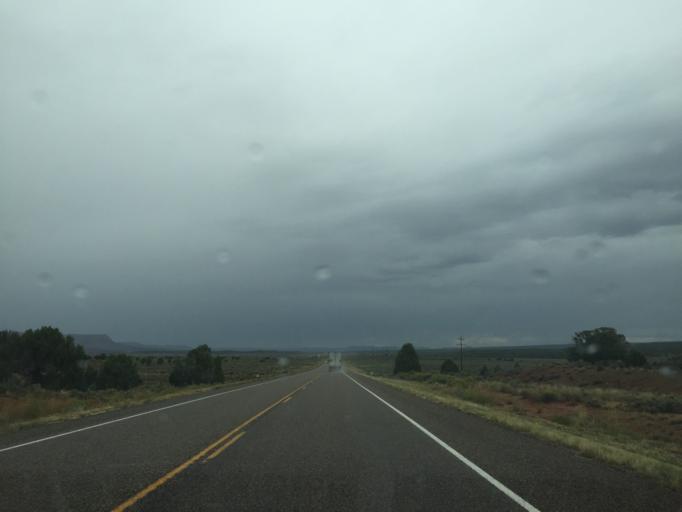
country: US
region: Utah
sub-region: Kane County
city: Kanab
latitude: 37.1067
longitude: -112.1234
